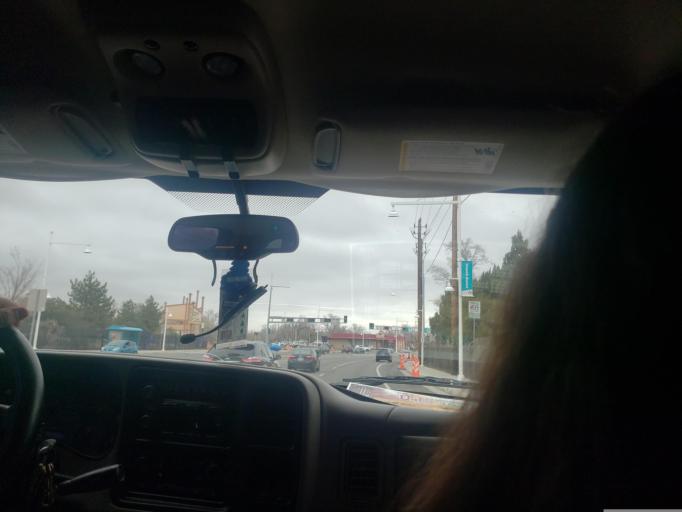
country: US
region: New Mexico
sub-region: Bernalillo County
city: Albuquerque
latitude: 35.0934
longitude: -106.6780
